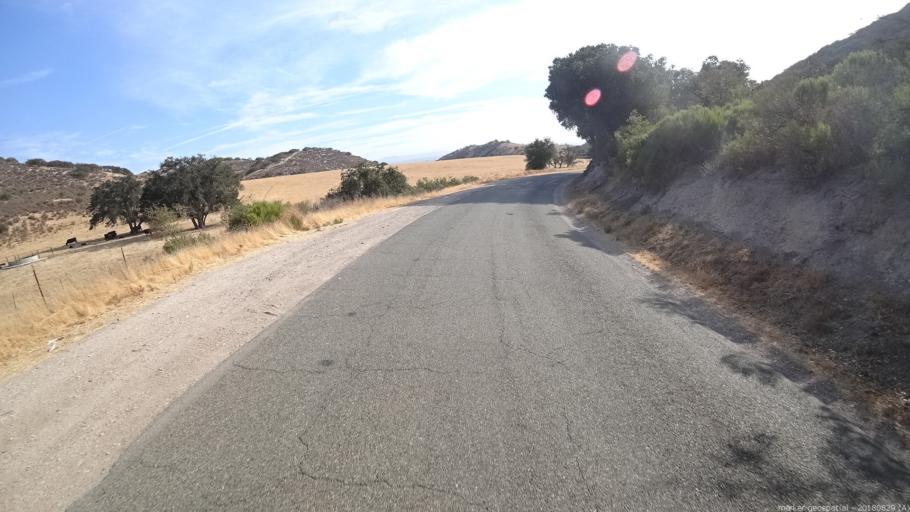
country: US
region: California
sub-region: Monterey County
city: King City
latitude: 36.0598
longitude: -121.0477
